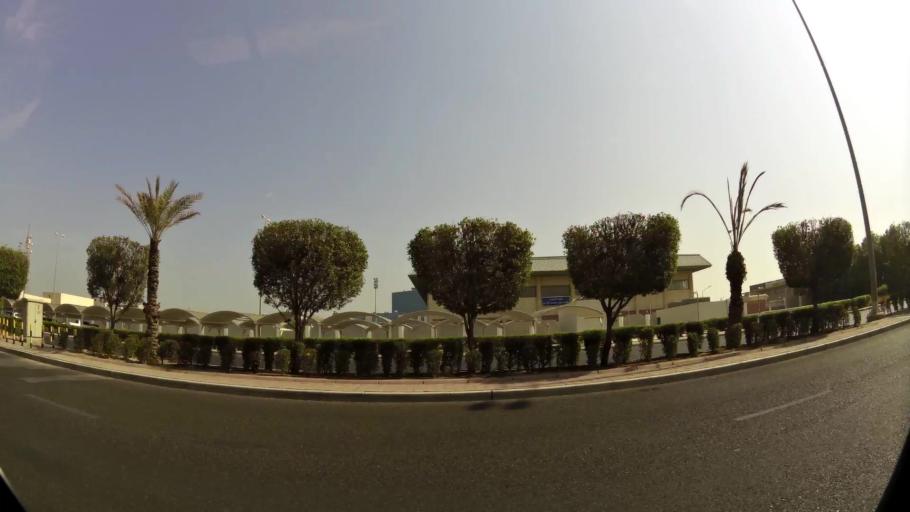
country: KW
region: Al Ahmadi
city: Al Fintas
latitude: 29.1655
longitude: 48.1232
